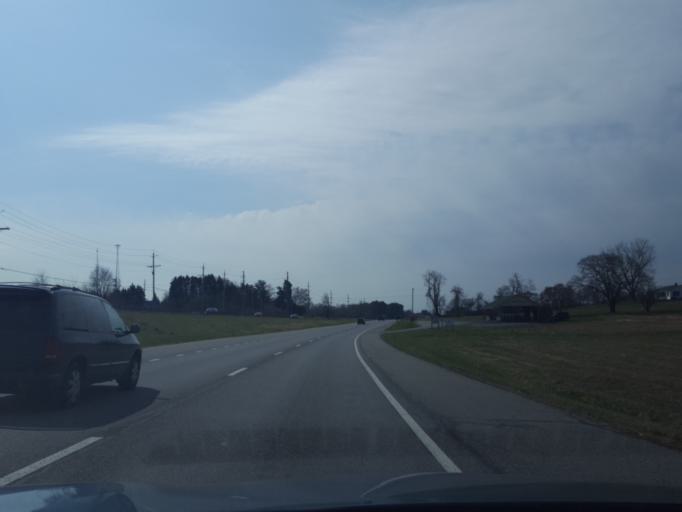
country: US
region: Maryland
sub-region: Calvert County
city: Dunkirk
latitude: 38.7356
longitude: -76.6590
